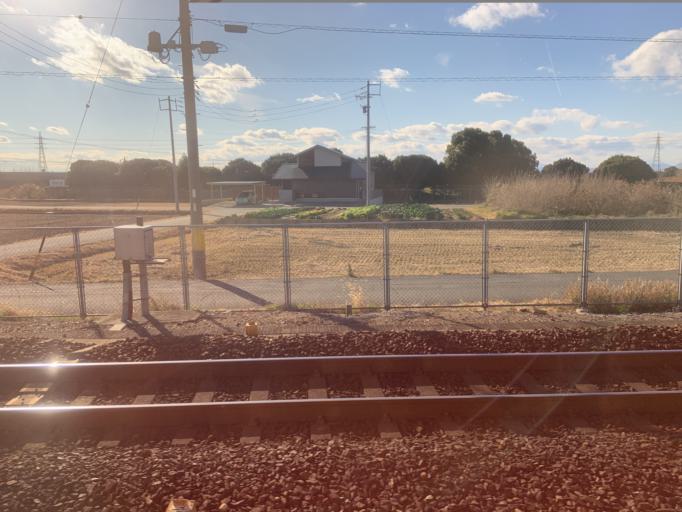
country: JP
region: Aichi
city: Inazawa
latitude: 35.2243
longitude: 136.8352
